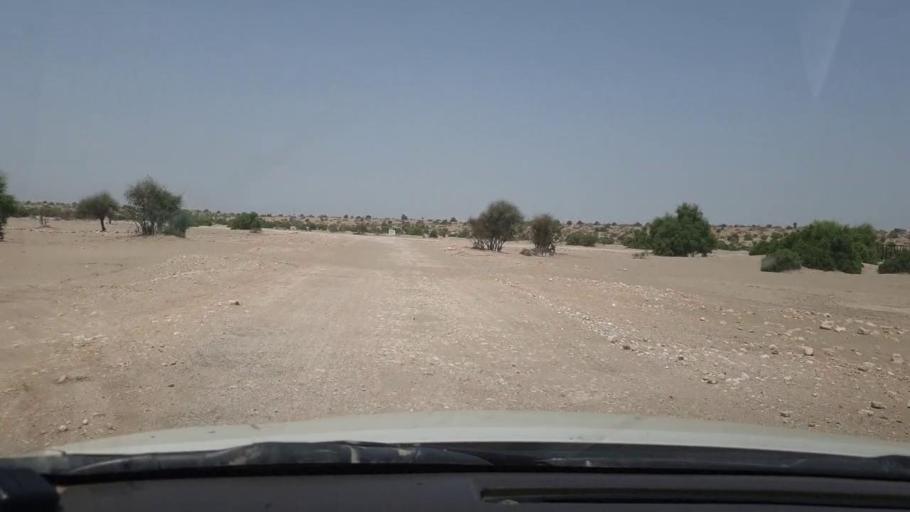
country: PK
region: Sindh
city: Kot Diji
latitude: 27.2843
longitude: 69.2344
